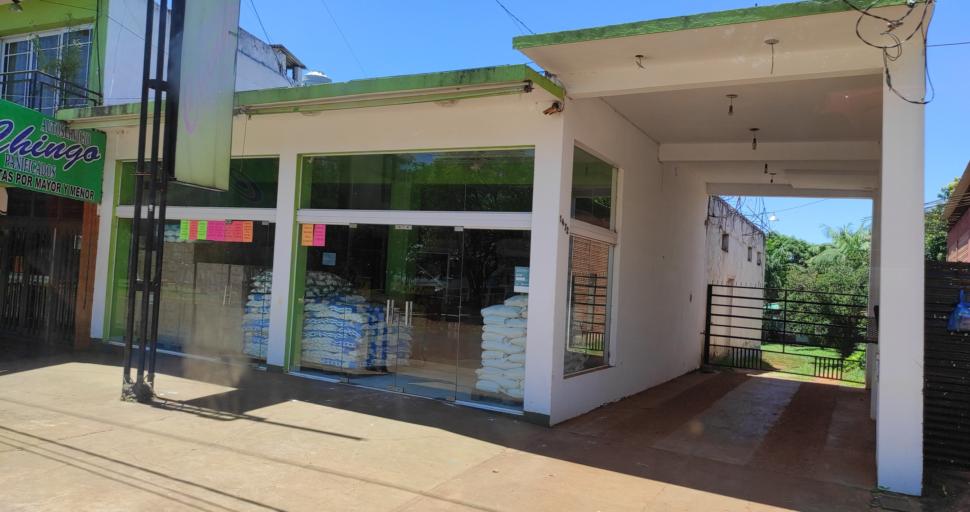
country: AR
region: Misiones
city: Dos de Mayo
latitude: -26.9926
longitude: -54.4794
